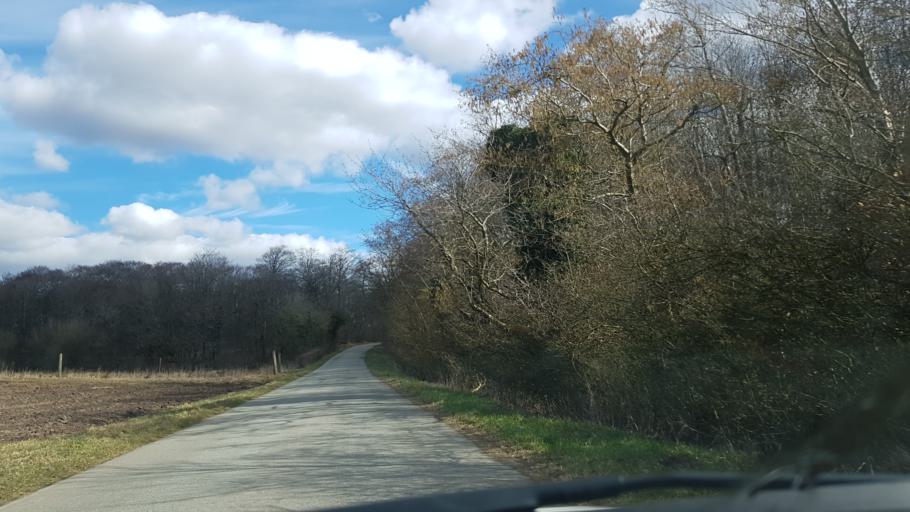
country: DK
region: South Denmark
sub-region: Kolding Kommune
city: Christiansfeld
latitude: 55.3569
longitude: 9.3784
